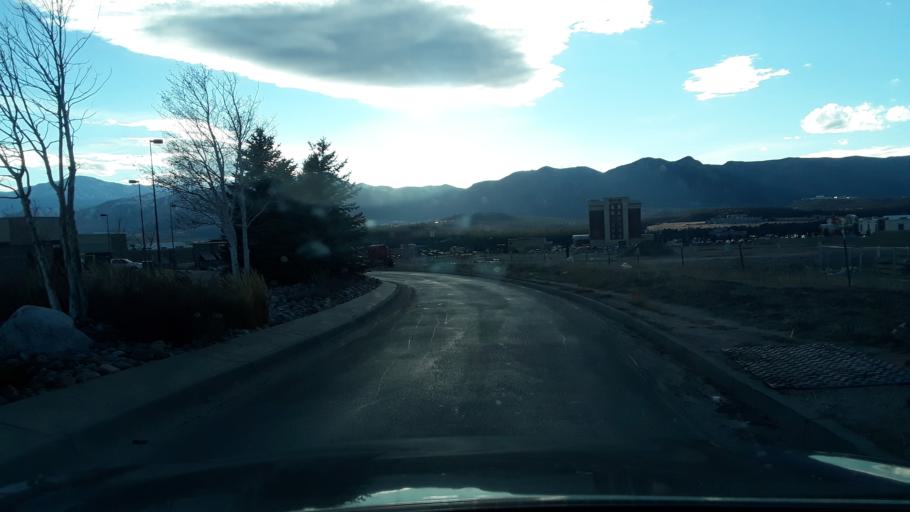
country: US
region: Colorado
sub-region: El Paso County
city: Gleneagle
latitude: 38.9925
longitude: -104.8040
